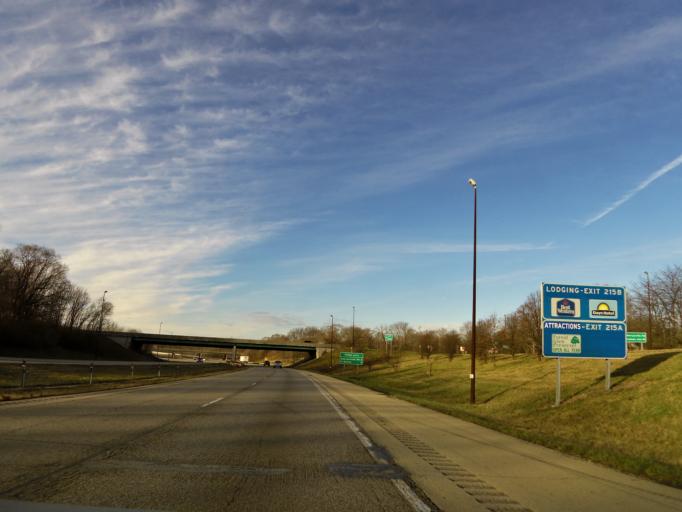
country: US
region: Illinois
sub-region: Vermilion County
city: Danville
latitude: 40.1142
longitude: -87.6084
